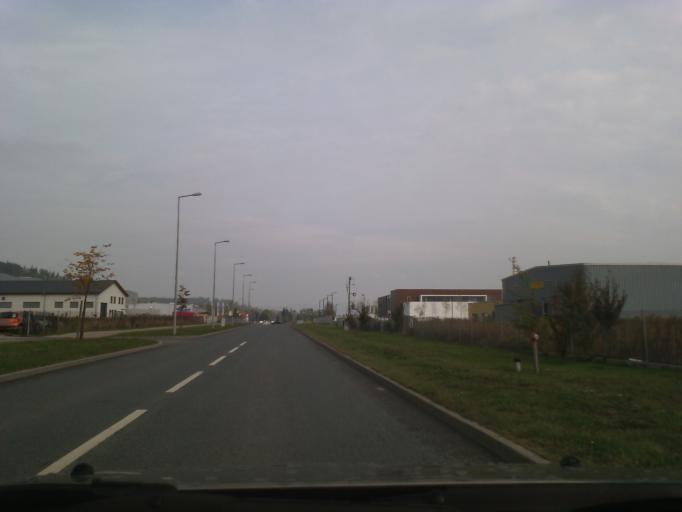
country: PL
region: Lower Silesian Voivodeship
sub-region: Jelenia Gora
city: Cieplice Slaskie Zdroj
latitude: 50.8832
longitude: 15.6977
